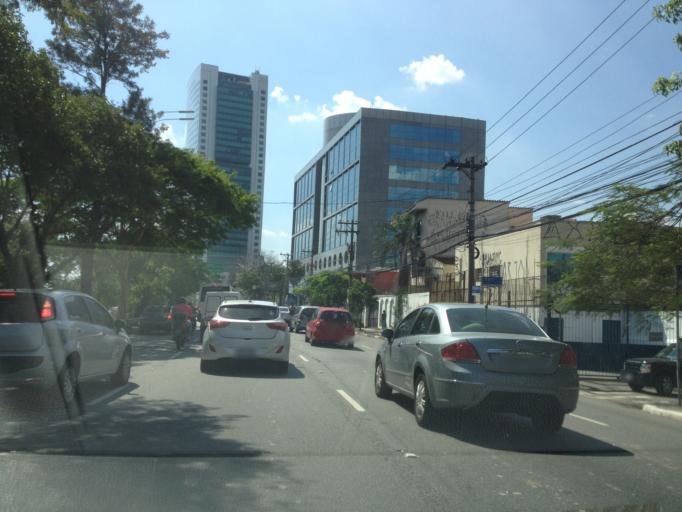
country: BR
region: Sao Paulo
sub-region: Sao Paulo
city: Sao Paulo
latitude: -23.5765
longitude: -46.6955
